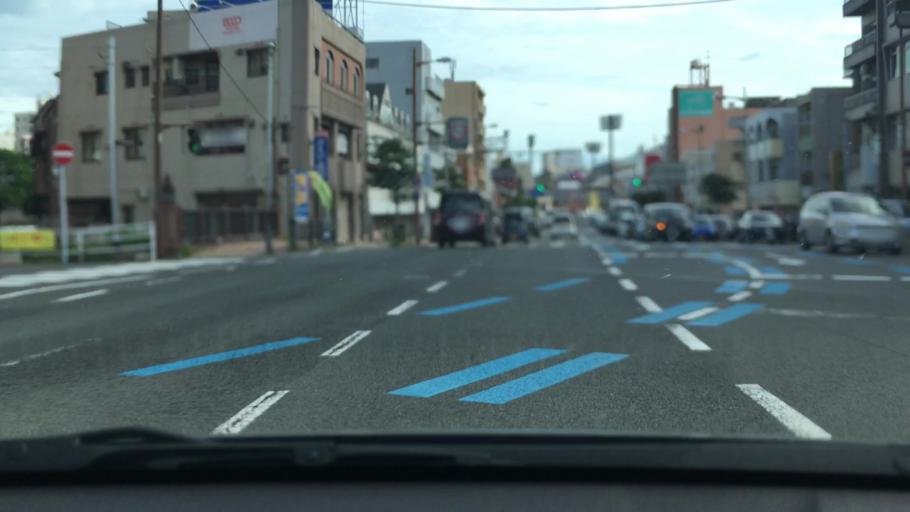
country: JP
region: Nagasaki
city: Nagasaki-shi
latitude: 32.7809
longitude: 129.8624
